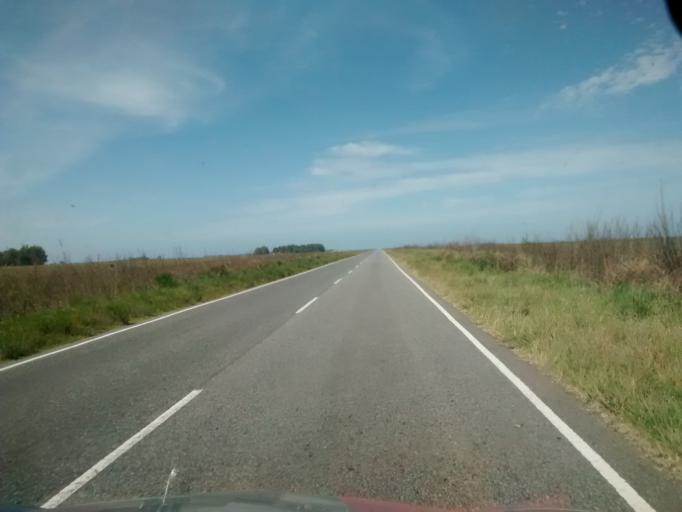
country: AR
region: Buenos Aires
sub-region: Partido de Rauch
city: Rauch
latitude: -36.4523
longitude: -58.5778
